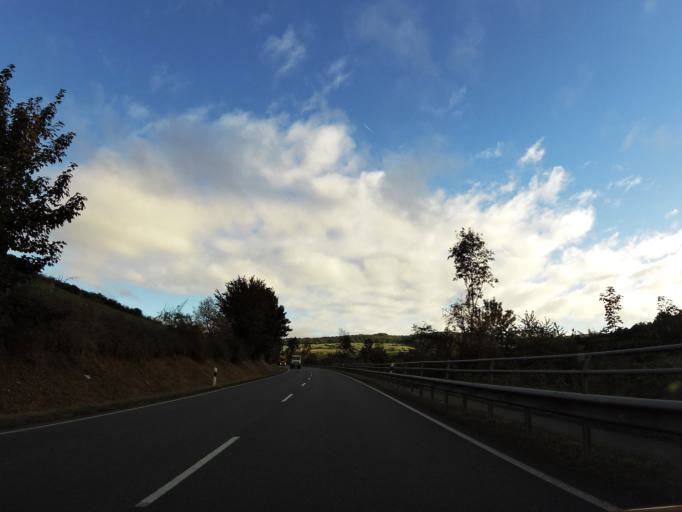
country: DE
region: Lower Saxony
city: Einbeck
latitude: 51.8367
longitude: 9.8375
